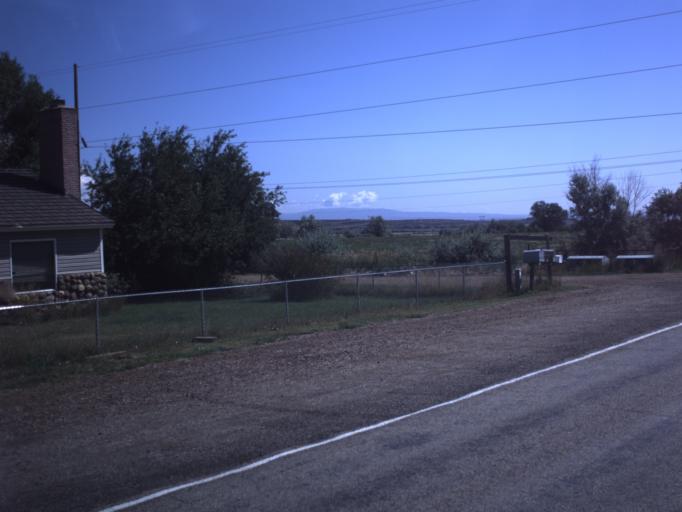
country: US
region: Utah
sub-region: Duchesne County
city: Roosevelt
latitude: 40.2580
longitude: -110.1623
